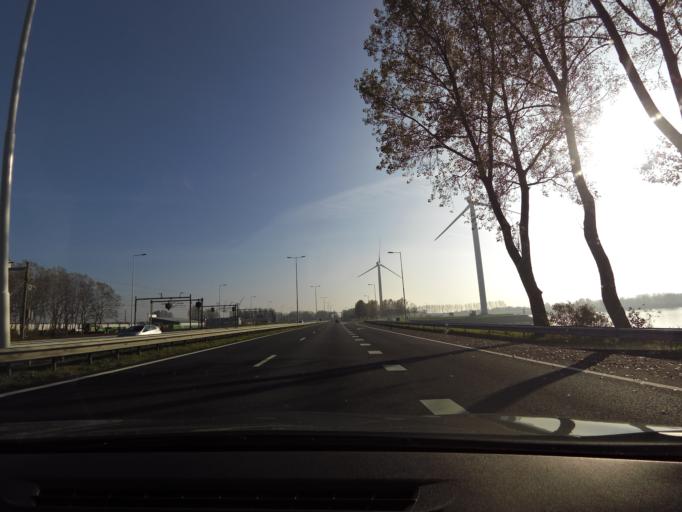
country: NL
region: South Holland
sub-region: Gemeente Brielle
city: Brielle
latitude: 51.9254
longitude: 4.1734
